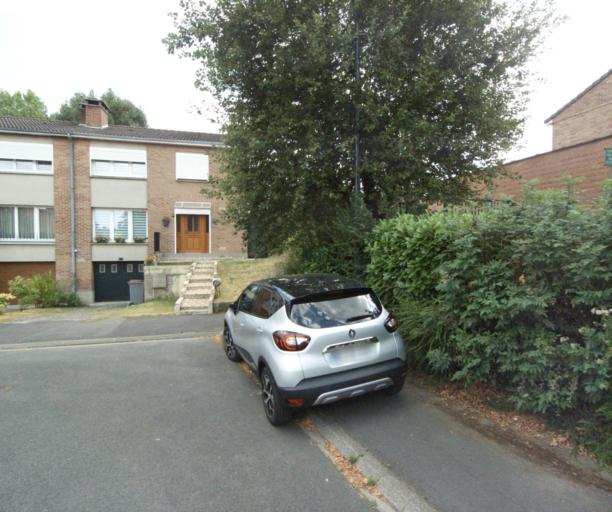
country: FR
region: Nord-Pas-de-Calais
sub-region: Departement du Nord
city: Neuville-en-Ferrain
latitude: 50.7502
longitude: 3.1603
